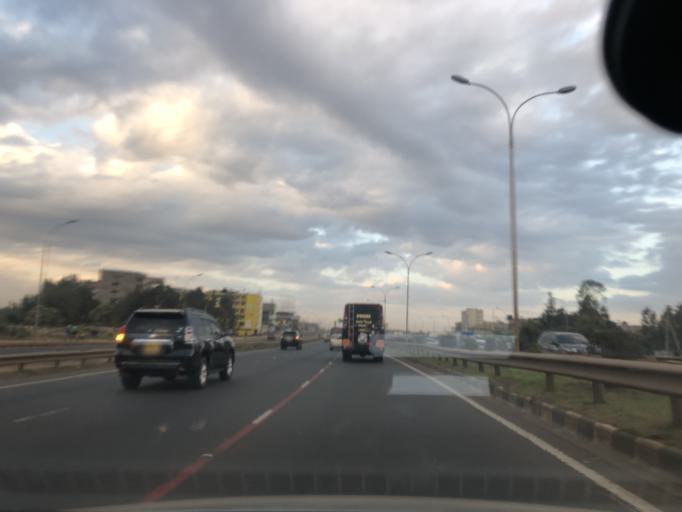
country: KE
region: Kiambu
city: Kiambu
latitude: -1.2089
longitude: 36.9120
